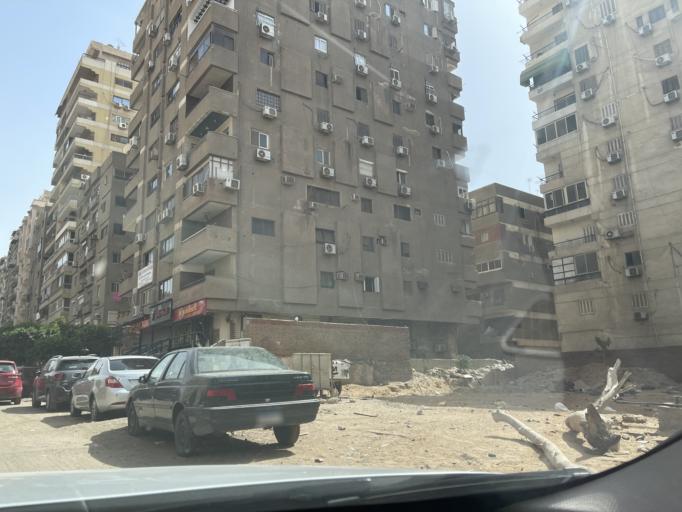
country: EG
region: Muhafazat al Qahirah
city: Cairo
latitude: 30.0651
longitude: 31.3502
